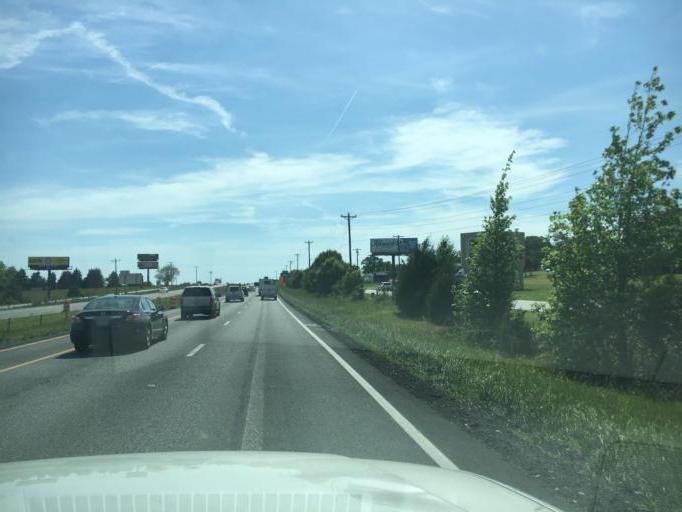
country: US
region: South Carolina
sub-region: Cherokee County
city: Gaffney
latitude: 35.0930
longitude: -81.6877
